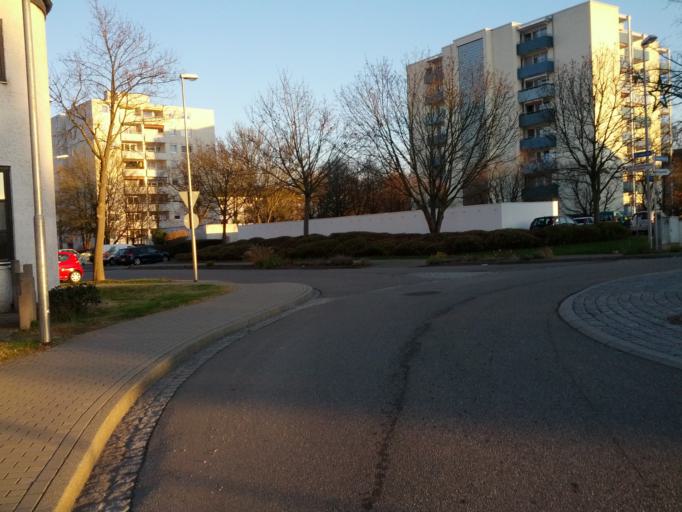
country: DE
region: Baden-Wuerttemberg
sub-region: Freiburg Region
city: Breisach am Rhein
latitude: 48.0359
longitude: 7.5871
